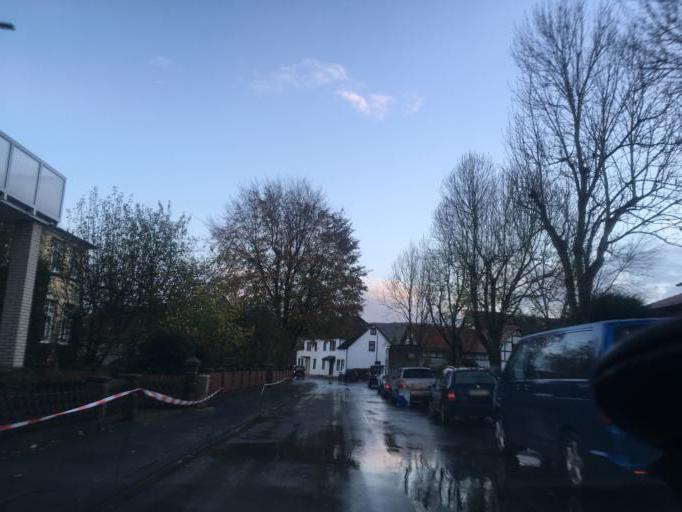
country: DE
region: Lower Saxony
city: Uslar
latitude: 51.6295
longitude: 9.6205
